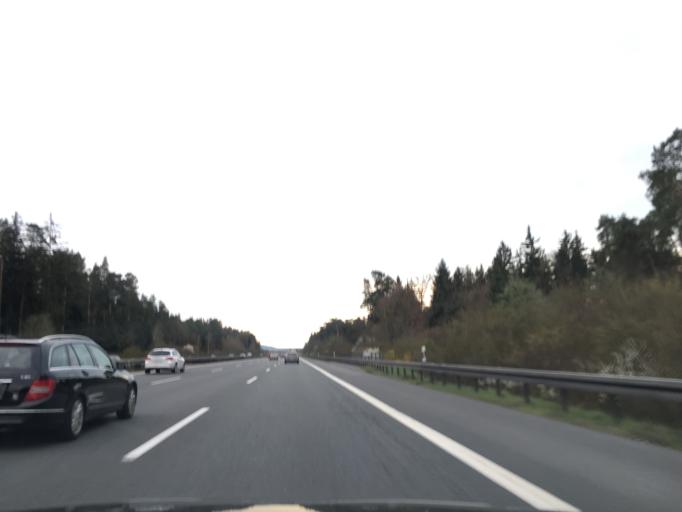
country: DE
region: Bavaria
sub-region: Regierungsbezirk Mittelfranken
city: Neunkirchen am Sand
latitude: 49.5451
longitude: 11.3204
